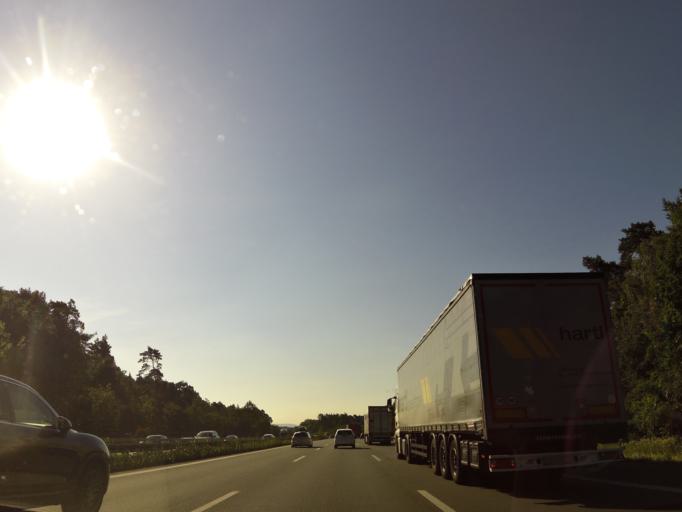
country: DE
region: Bavaria
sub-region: Regierungsbezirk Mittelfranken
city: Heroldsberg
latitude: 49.5033
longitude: 11.1252
